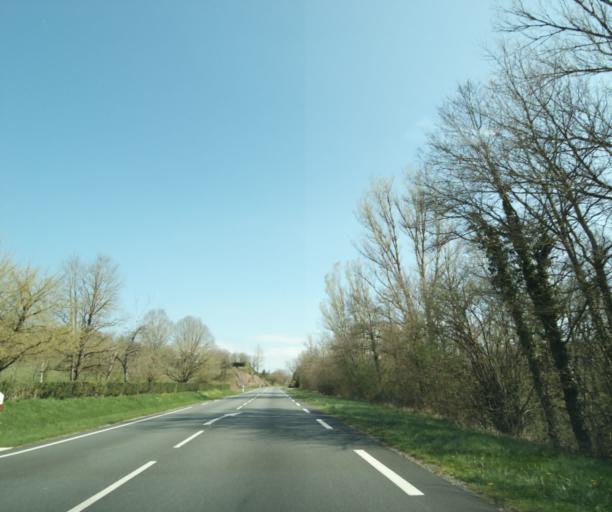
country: FR
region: Midi-Pyrenees
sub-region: Departement de l'Aveyron
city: La Loubiere
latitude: 44.3738
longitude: 2.6514
